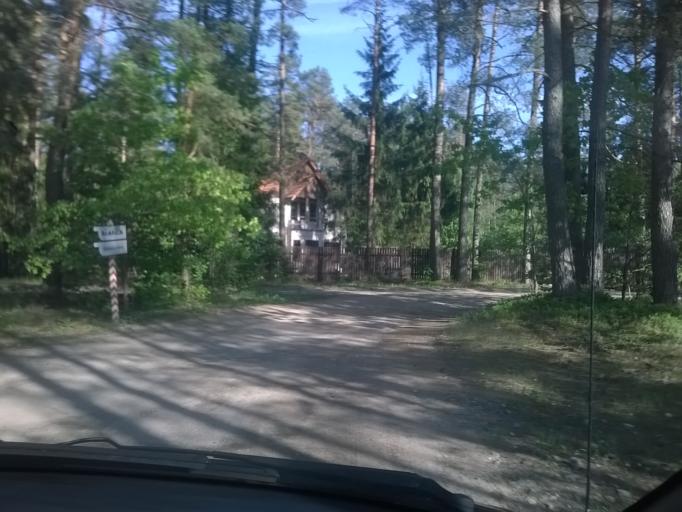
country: LV
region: Seja
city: Loja
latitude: 57.1228
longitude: 24.6590
